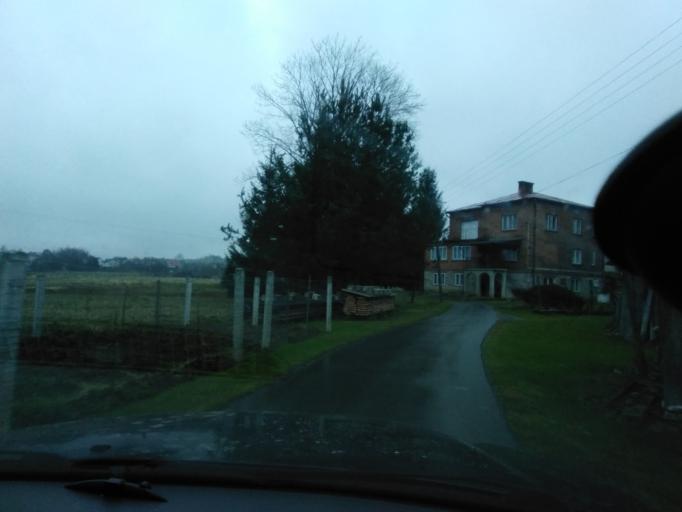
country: PL
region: Subcarpathian Voivodeship
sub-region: Powiat brzozowski
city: Stara Wies
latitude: 49.7318
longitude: 21.9939
